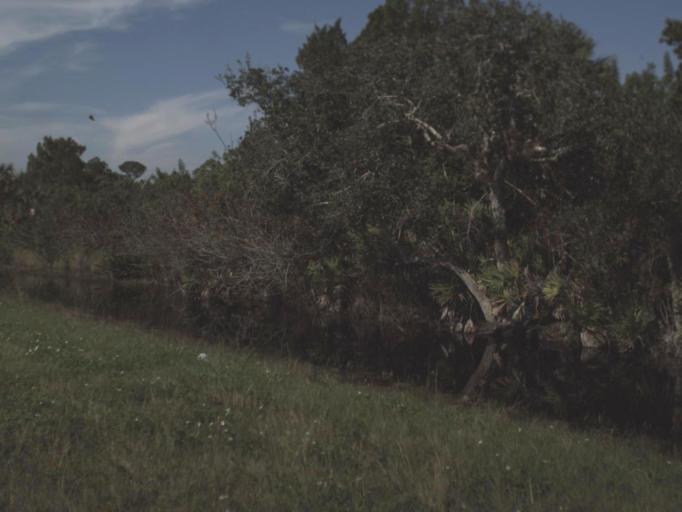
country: US
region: Florida
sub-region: Brevard County
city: Titusville
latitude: 28.6436
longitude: -80.7480
